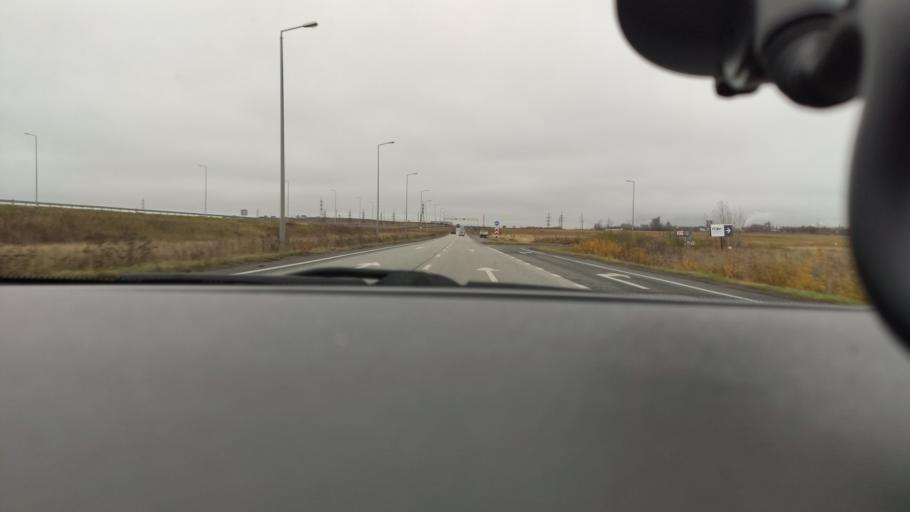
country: RU
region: Perm
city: Kondratovo
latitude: 57.9275
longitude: 56.1709
